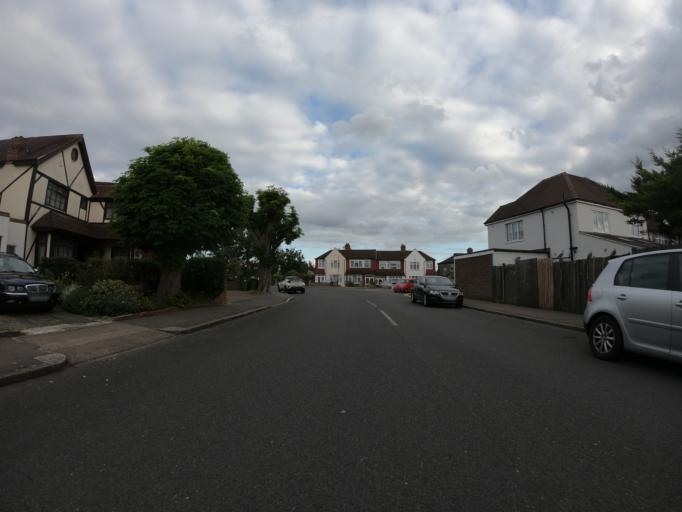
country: GB
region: England
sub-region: Greater London
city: Bexleyheath
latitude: 51.4806
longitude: 0.1326
